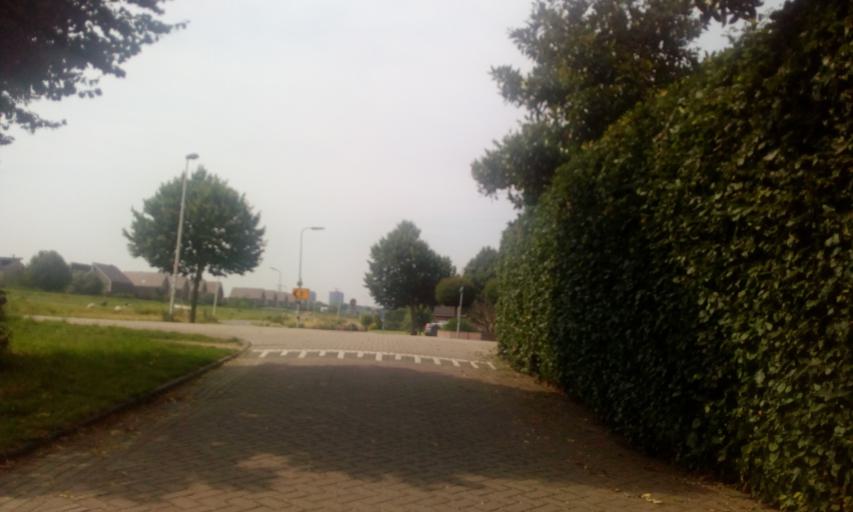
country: NL
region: South Holland
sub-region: Gemeente Krimpen aan den IJssel
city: Krimpen aan den IJssel
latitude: 51.9568
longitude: 4.6123
